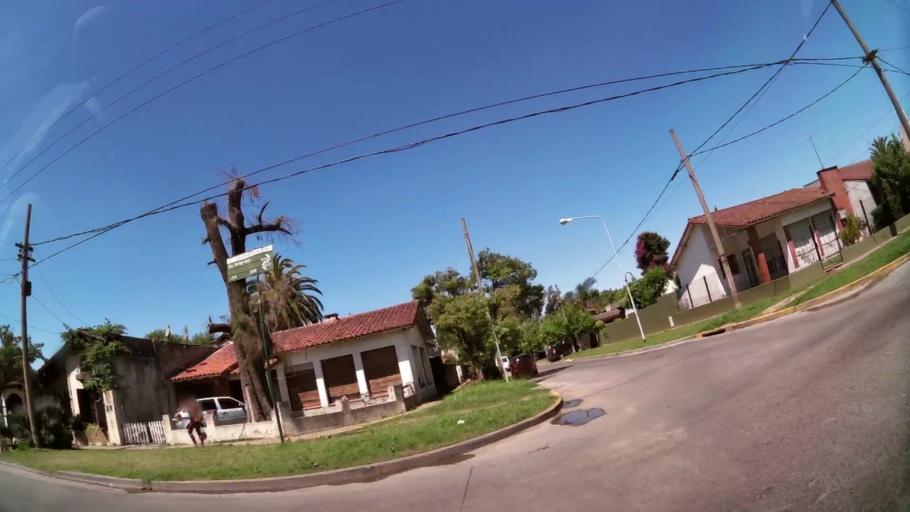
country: AR
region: Buenos Aires
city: Hurlingham
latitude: -34.4930
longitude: -58.6538
